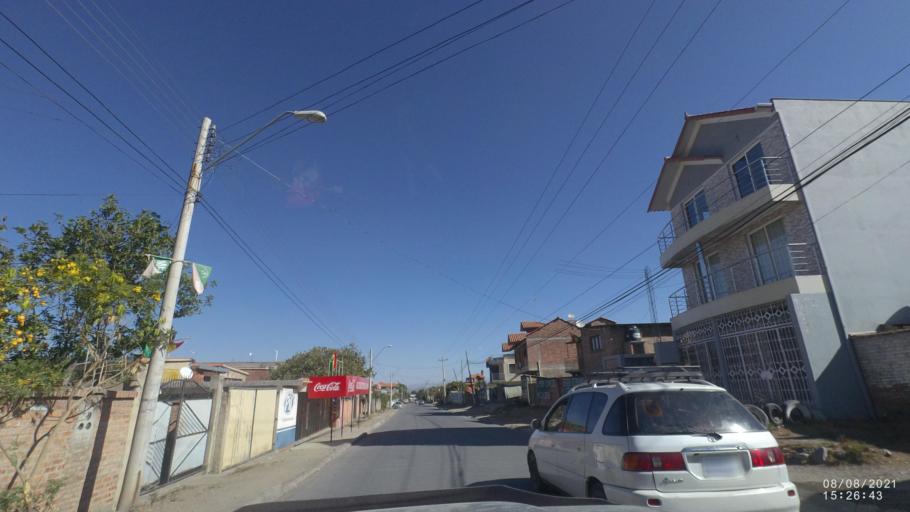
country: BO
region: Cochabamba
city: Cochabamba
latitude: -17.3259
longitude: -66.2822
